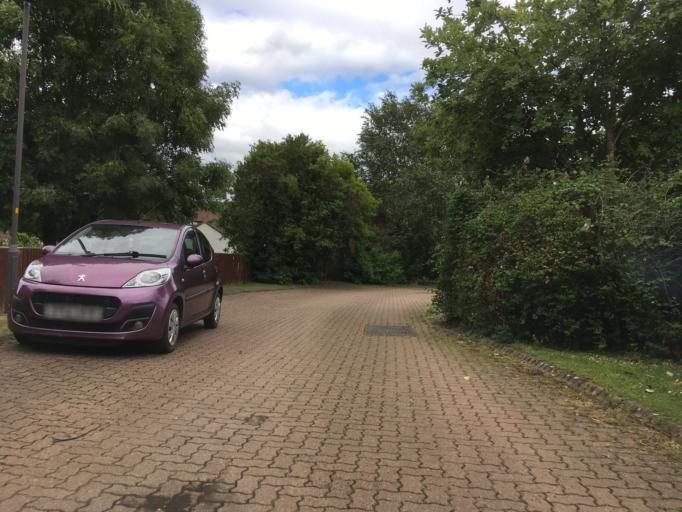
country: GB
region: England
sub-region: Gloucestershire
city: Cinderford
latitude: 51.7971
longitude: -2.4253
